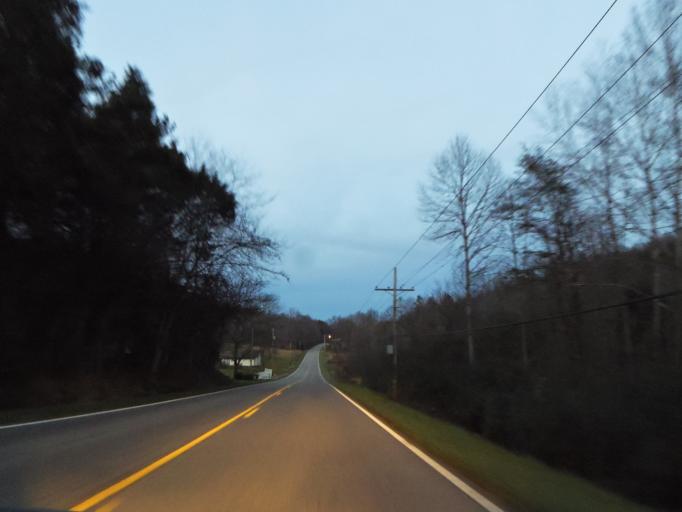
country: US
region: Tennessee
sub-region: Morgan County
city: Coalfield
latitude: 35.9838
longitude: -84.4341
